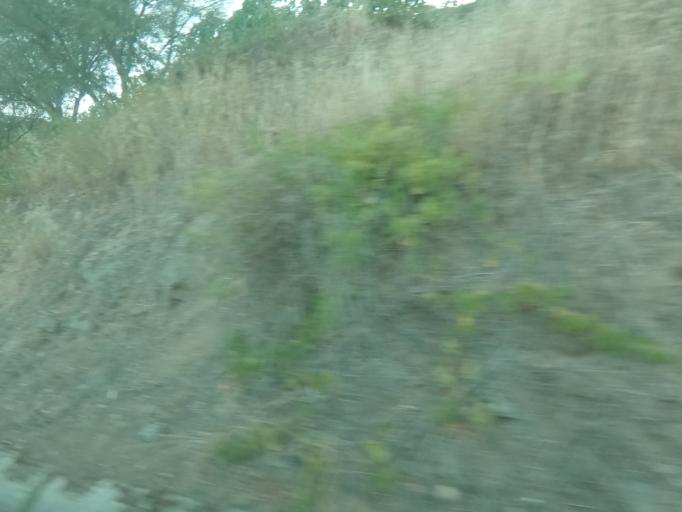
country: PT
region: Vila Real
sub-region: Peso da Regua
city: Peso da Regua
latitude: 41.1407
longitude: -7.7401
